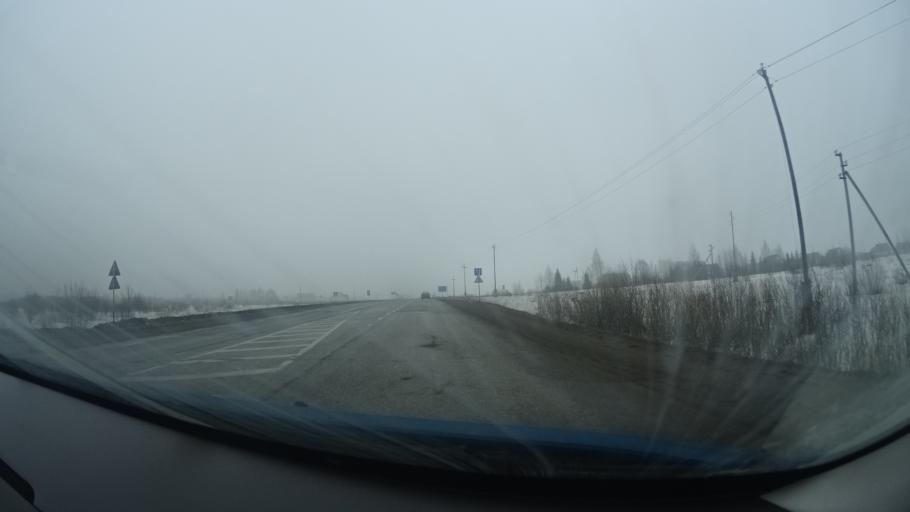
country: RU
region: Perm
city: Kuyeda
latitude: 56.4480
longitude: 55.5988
